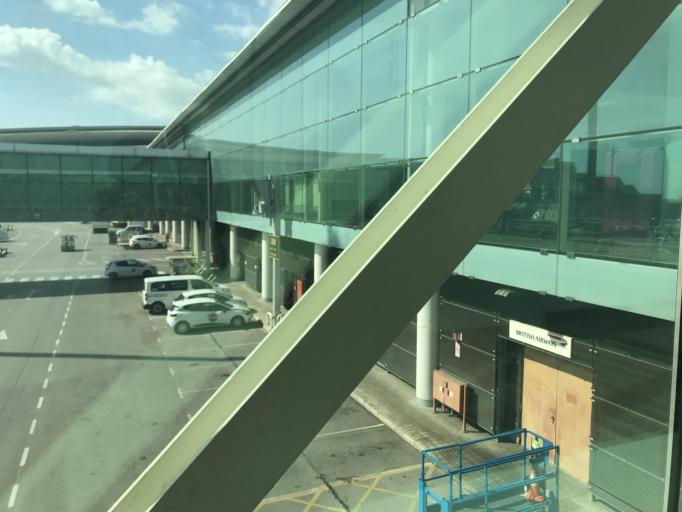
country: ES
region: Catalonia
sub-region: Provincia de Barcelona
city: El Prat de Llobregat
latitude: 41.2902
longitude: 2.0777
